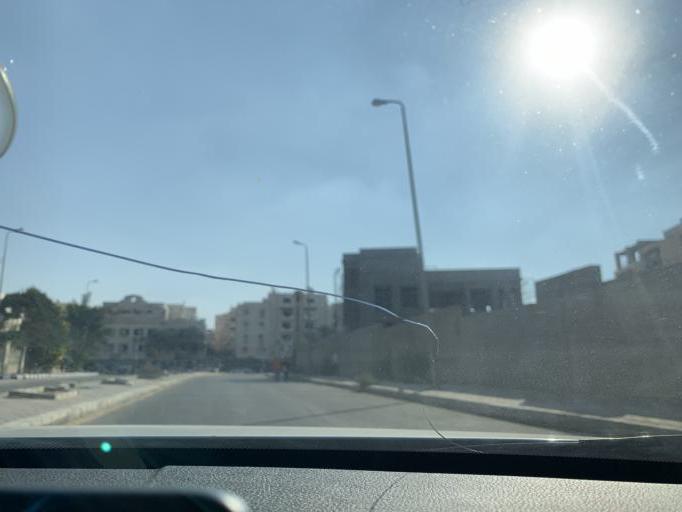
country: EG
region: Muhafazat al Qalyubiyah
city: Al Khankah
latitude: 30.0197
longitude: 31.4792
